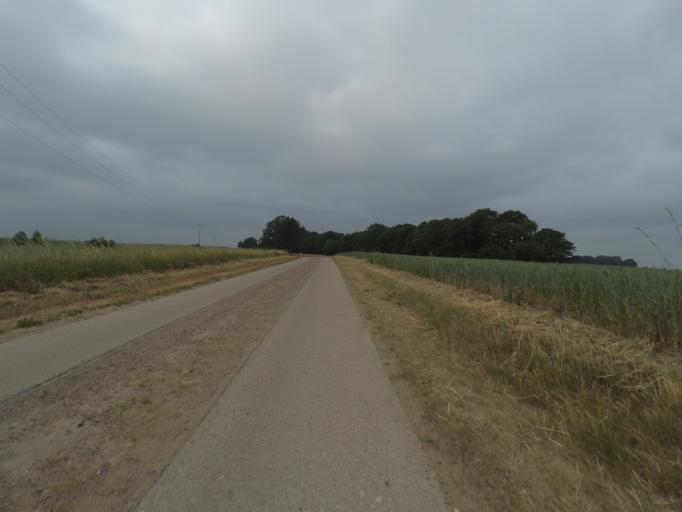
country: DE
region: Mecklenburg-Vorpommern
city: Goldberg
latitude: 53.5184
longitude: 12.0944
